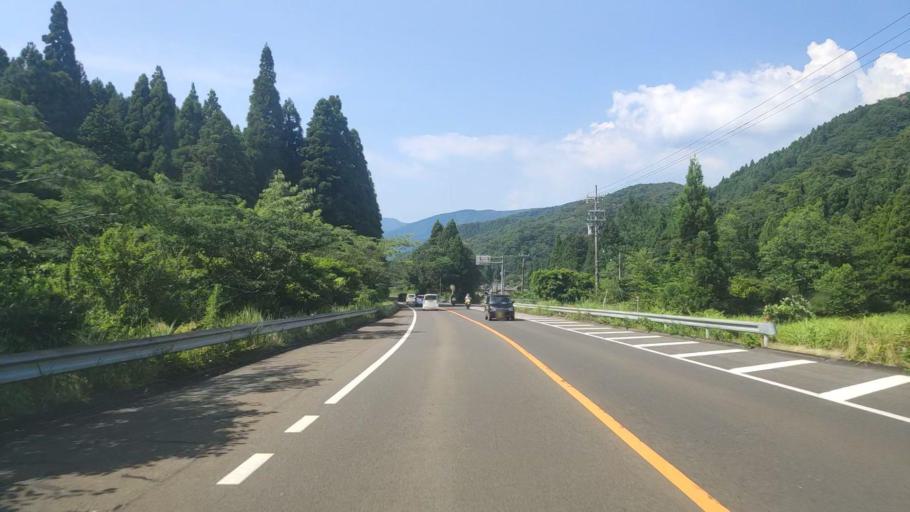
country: JP
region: Fukui
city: Tsuruga
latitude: 35.5830
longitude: 136.1245
